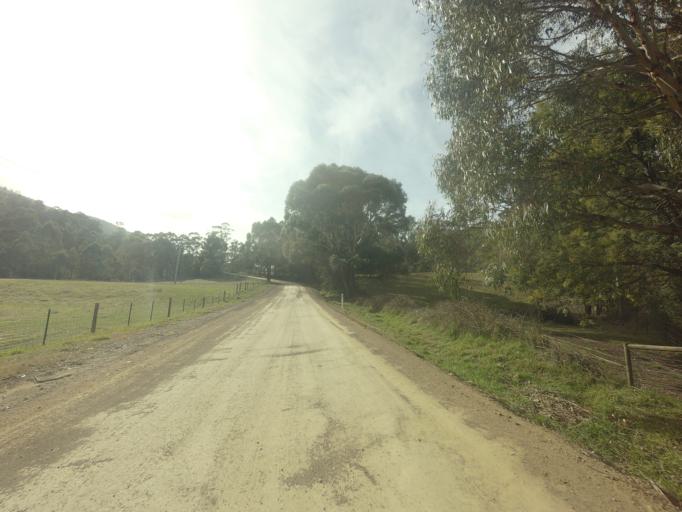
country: AU
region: Tasmania
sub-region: Huon Valley
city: Huonville
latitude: -43.0725
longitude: 147.0832
